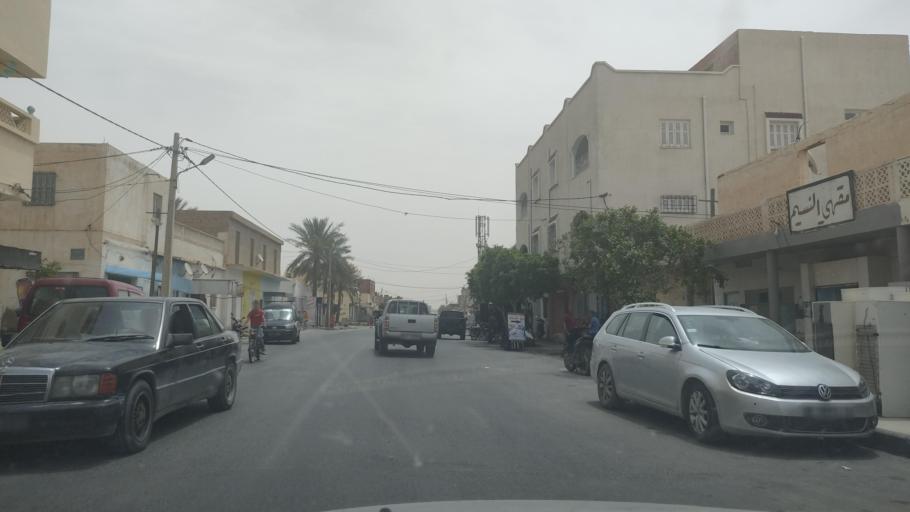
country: TN
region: Gafsa
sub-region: Gafsa Municipality
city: Gafsa
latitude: 34.3392
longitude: 8.9512
